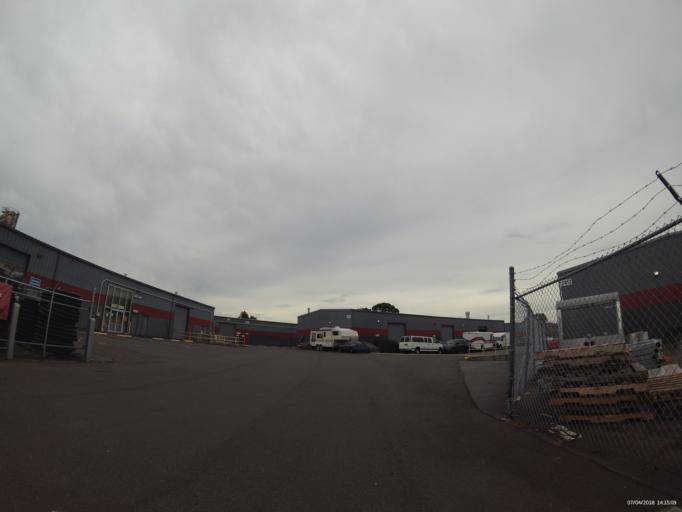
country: US
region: Washington
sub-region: Pierce County
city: McChord Air Force Base
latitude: 47.1599
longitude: -122.4818
